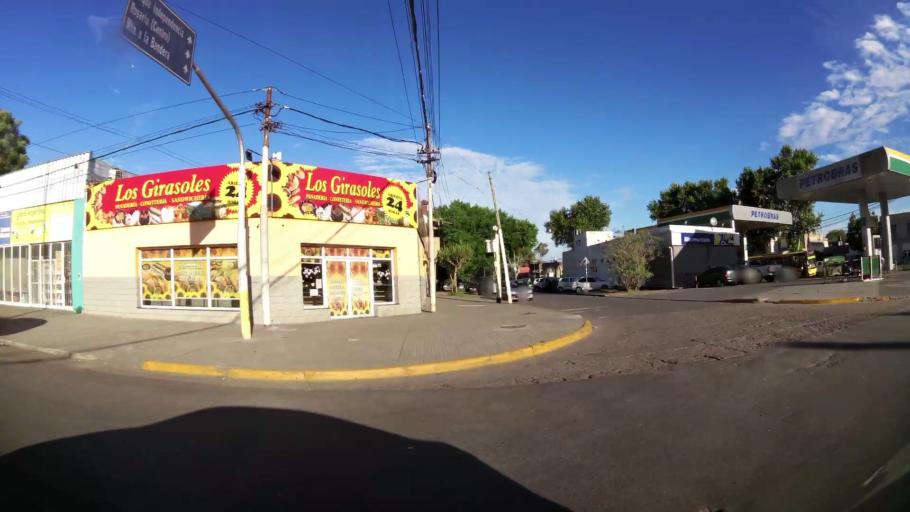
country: AR
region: Santa Fe
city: Gobernador Galvez
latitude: -32.9910
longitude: -60.6732
